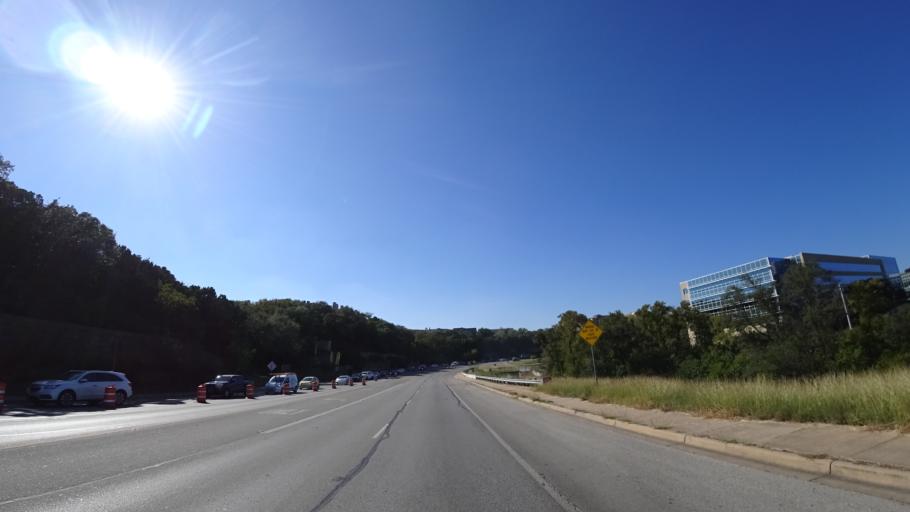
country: US
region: Texas
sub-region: Travis County
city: Rollingwood
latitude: 30.2668
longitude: -97.7837
